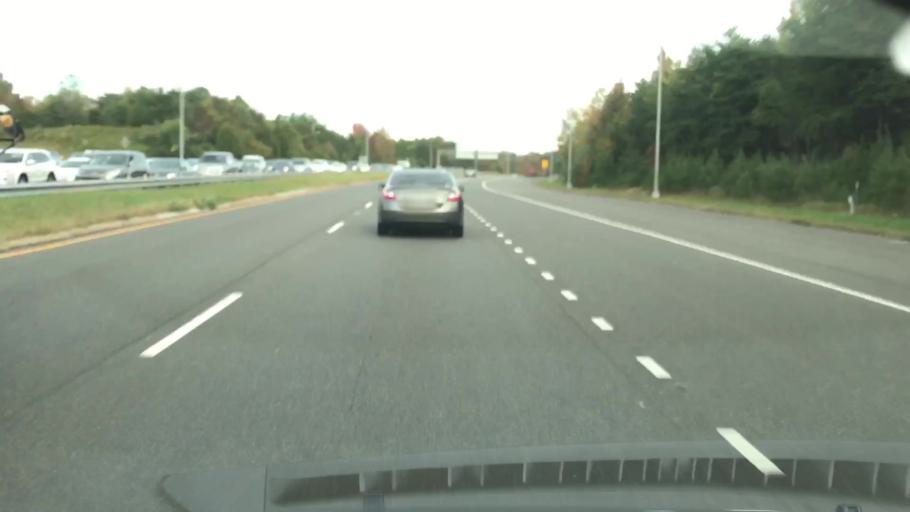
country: US
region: Virginia
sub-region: Fairfax County
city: West Springfield
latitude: 38.7593
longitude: -77.2167
